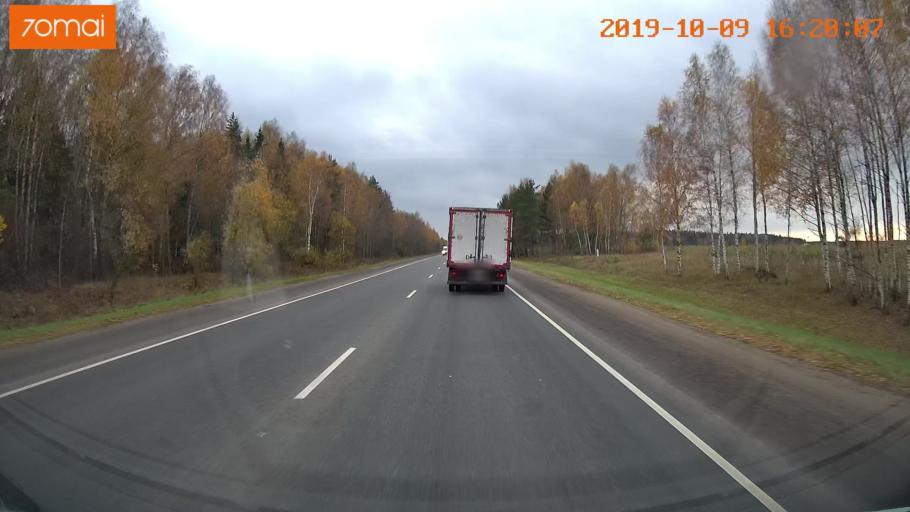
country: RU
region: Kostroma
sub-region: Kostromskoy Rayon
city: Kostroma
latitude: 57.7105
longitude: 40.8930
